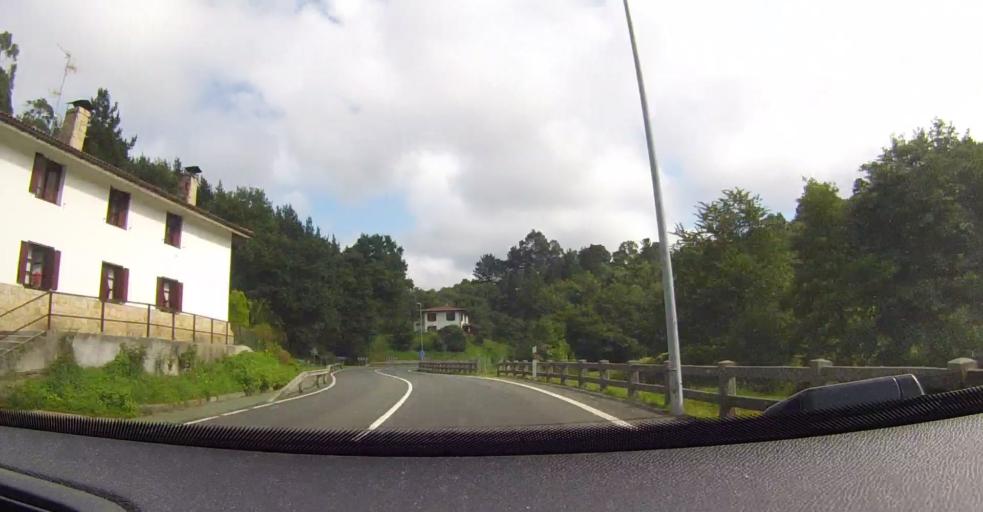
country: ES
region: Basque Country
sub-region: Bizkaia
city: Ibarrangelu
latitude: 43.3929
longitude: -2.6418
